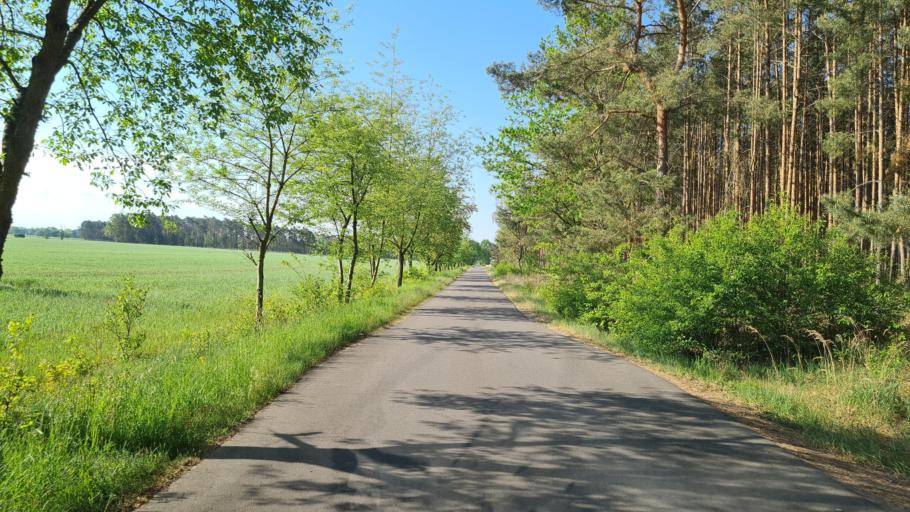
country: DE
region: Brandenburg
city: Falkenberg
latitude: 51.6091
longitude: 13.2048
